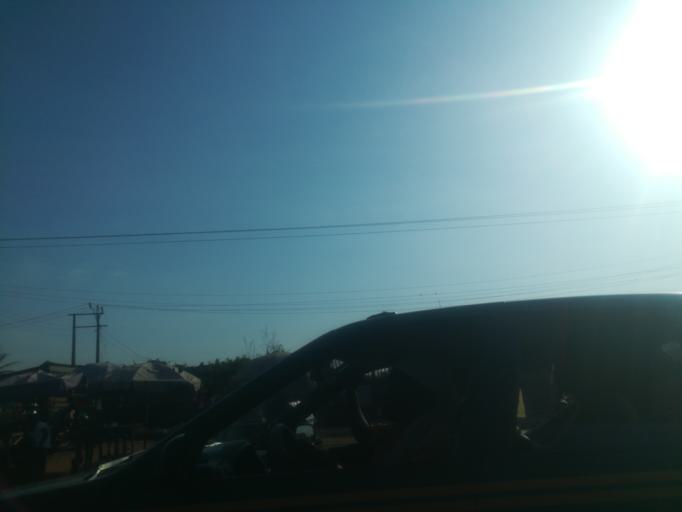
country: NG
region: Ogun
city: Abeokuta
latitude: 7.1818
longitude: 3.2812
